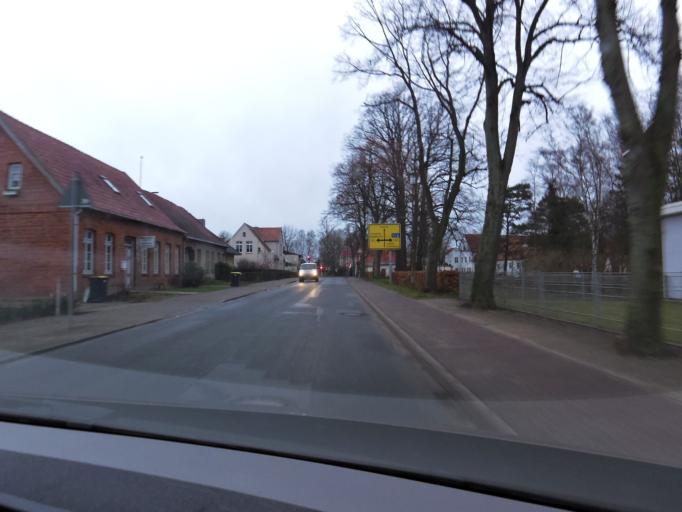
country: DE
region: Mecklenburg-Vorpommern
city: Rehna
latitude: 53.7789
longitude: 11.0521
